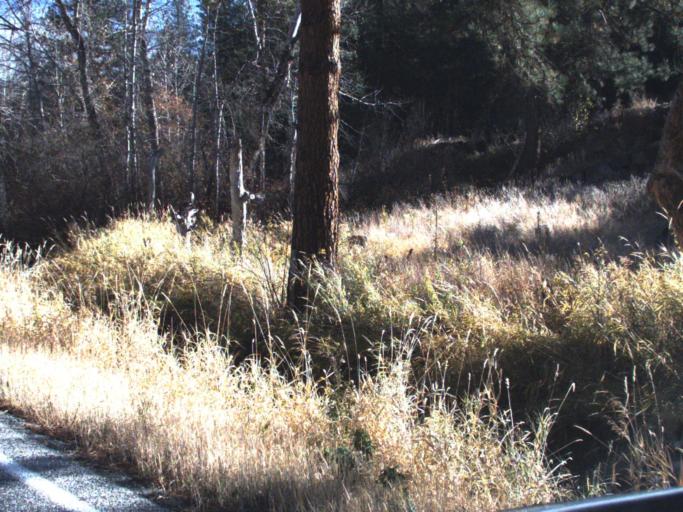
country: US
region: Washington
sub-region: Ferry County
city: Republic
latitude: 48.7817
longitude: -118.6271
